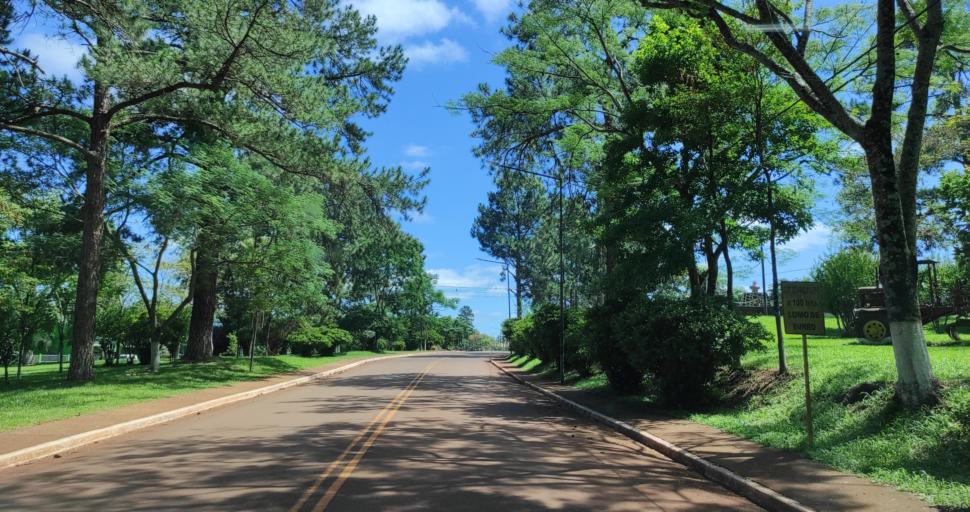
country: AR
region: Misiones
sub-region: Departamento de Veinticinco de Mayo
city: Veinticinco de Mayo
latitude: -27.3803
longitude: -54.7452
